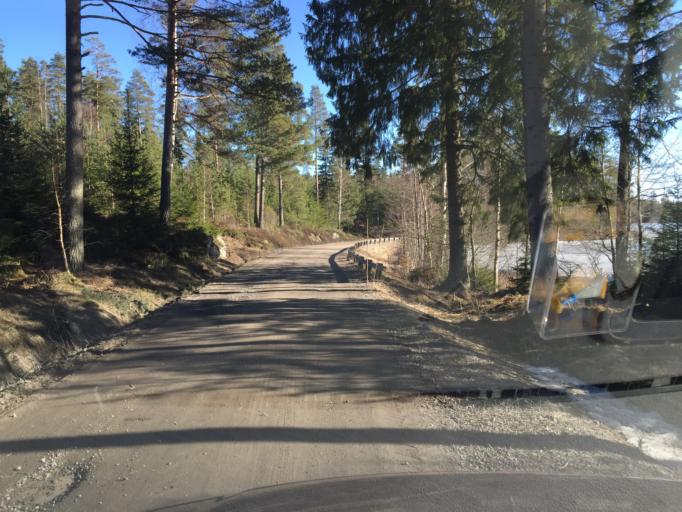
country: SE
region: OErebro
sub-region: Orebro Kommun
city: Odensbacken
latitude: 58.9900
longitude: 15.6247
